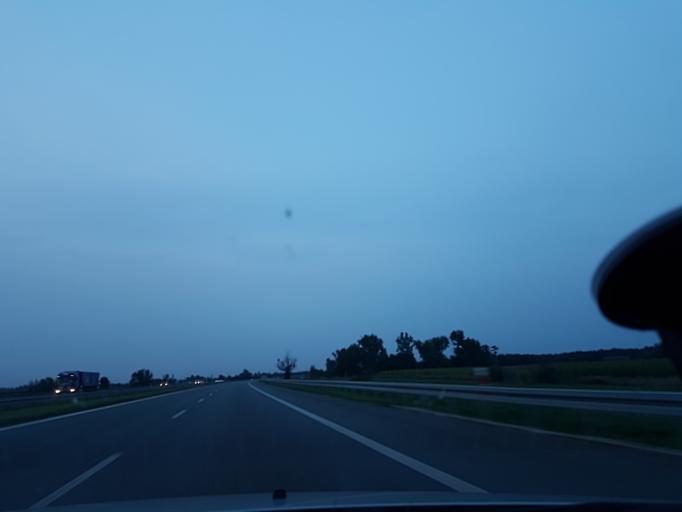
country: PL
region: Lodz Voivodeship
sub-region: Powiat leczycki
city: Piatek
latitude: 52.0393
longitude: 19.5415
